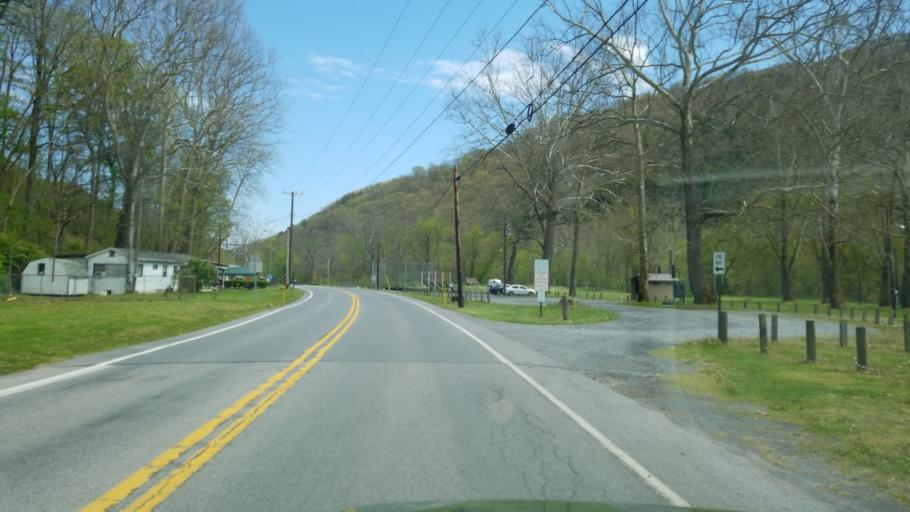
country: US
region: Pennsylvania
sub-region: Huntingdon County
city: Mount Union
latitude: 40.3946
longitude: -77.9378
